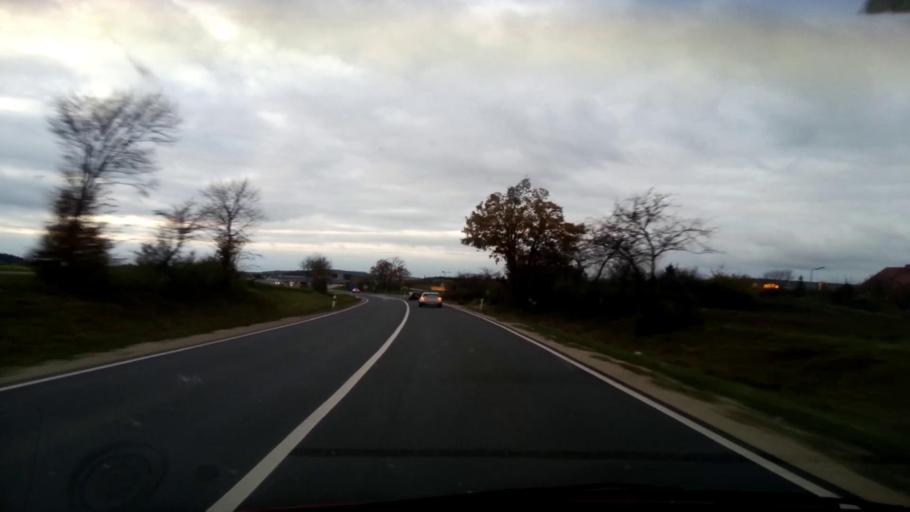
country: DE
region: Bavaria
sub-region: Upper Franconia
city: Niederfullbach
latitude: 50.2206
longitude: 11.0578
